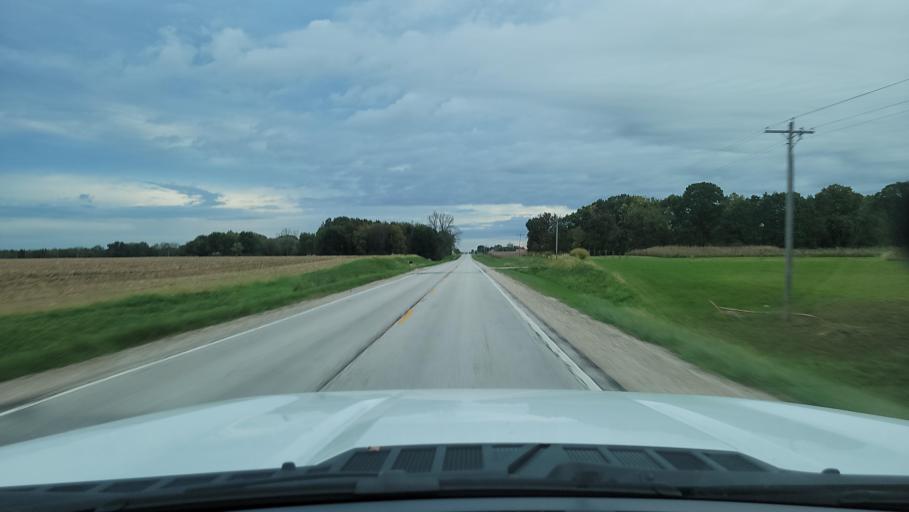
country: US
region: Illinois
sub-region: Schuyler County
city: Rushville
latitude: 40.0532
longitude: -90.6152
